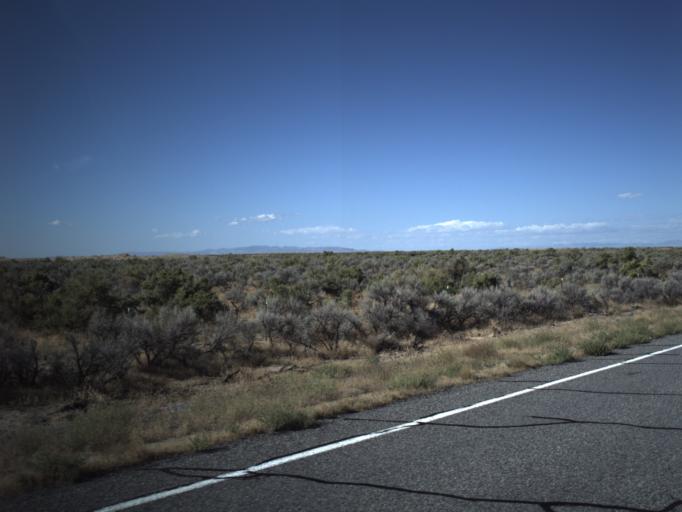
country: US
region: Utah
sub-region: Millard County
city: Delta
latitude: 39.3540
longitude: -112.4367
